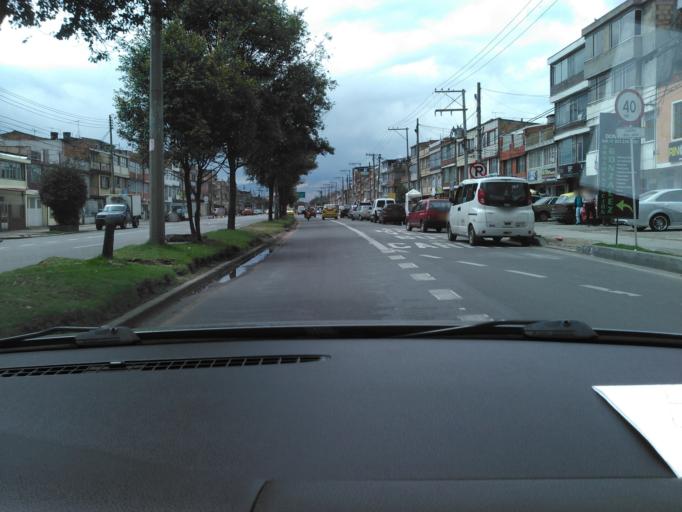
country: CO
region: Bogota D.C.
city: Bogota
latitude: 4.6182
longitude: -74.1133
